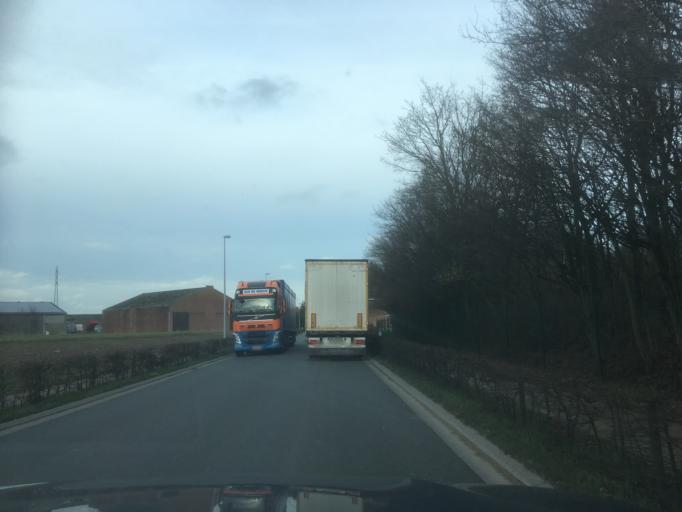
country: BE
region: Flanders
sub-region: Provincie West-Vlaanderen
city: Oostrozebeke
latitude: 50.9124
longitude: 3.3533
